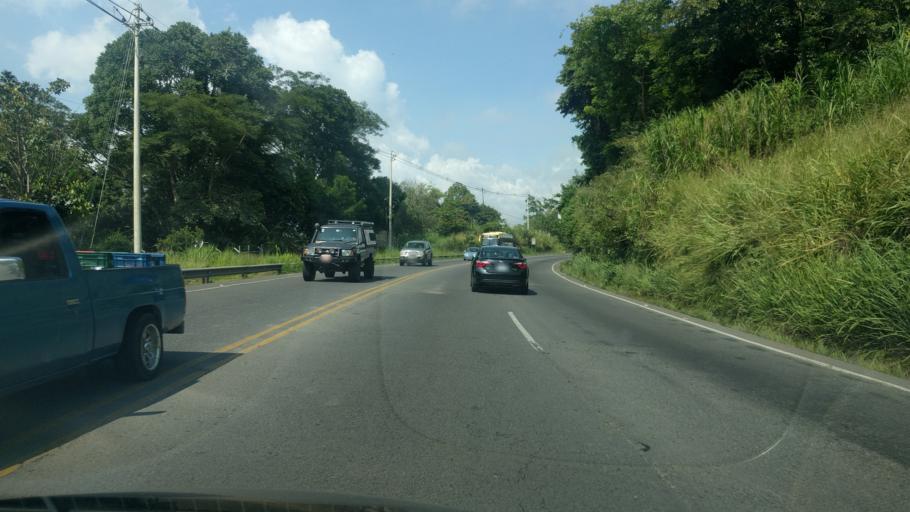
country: CR
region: Alajuela
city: Carrillos
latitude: 10.0052
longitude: -84.2982
